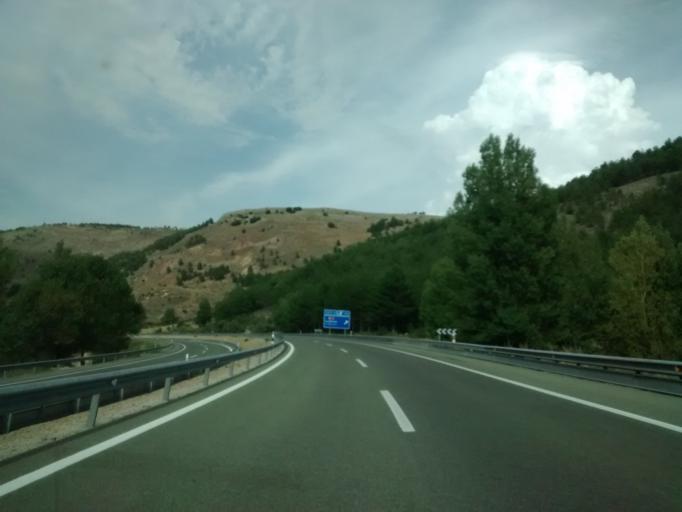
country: ES
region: Castille and Leon
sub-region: Provincia de Soria
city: Medinaceli
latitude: 41.1759
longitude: -2.4013
